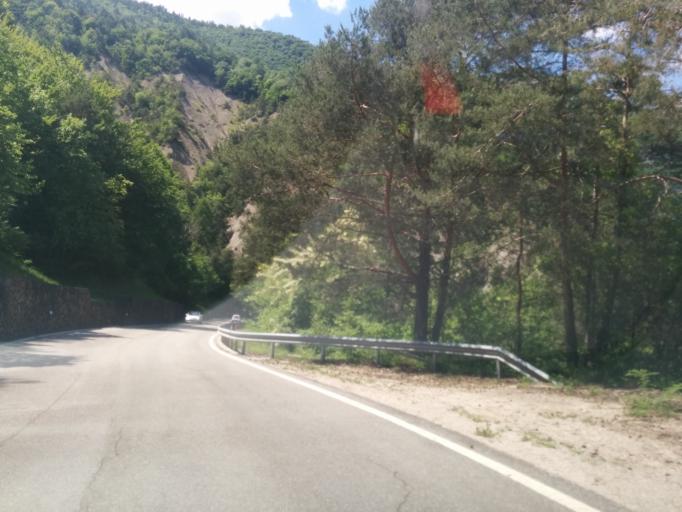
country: IT
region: Trentino-Alto Adige
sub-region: Provincia di Trento
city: Terres
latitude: 46.3161
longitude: 11.0178
